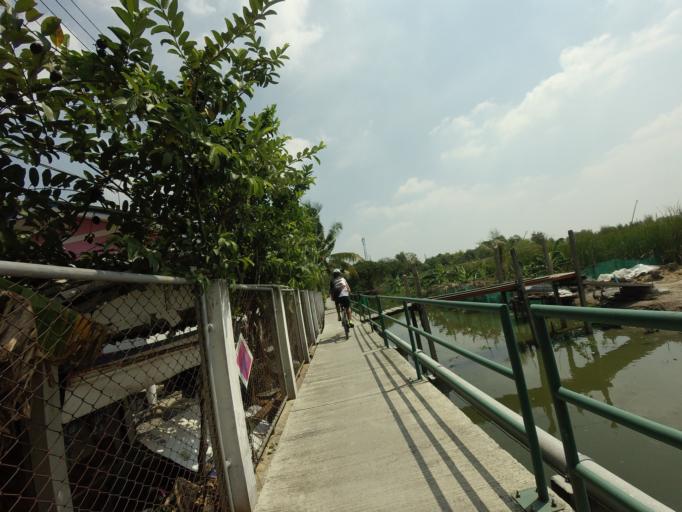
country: TH
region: Bangkok
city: Saphan Sung
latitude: 13.7535
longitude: 100.6755
